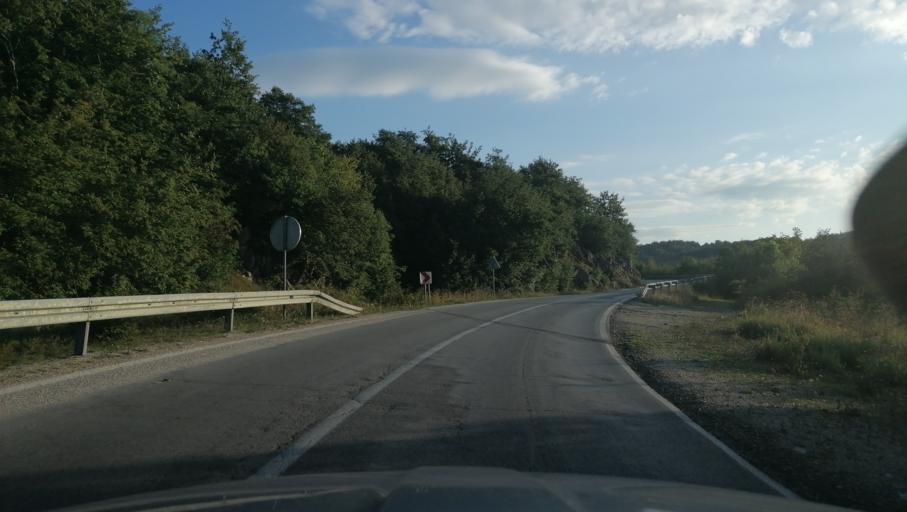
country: BA
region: Federation of Bosnia and Herzegovina
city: Prozor
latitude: 43.8388
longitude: 17.5907
